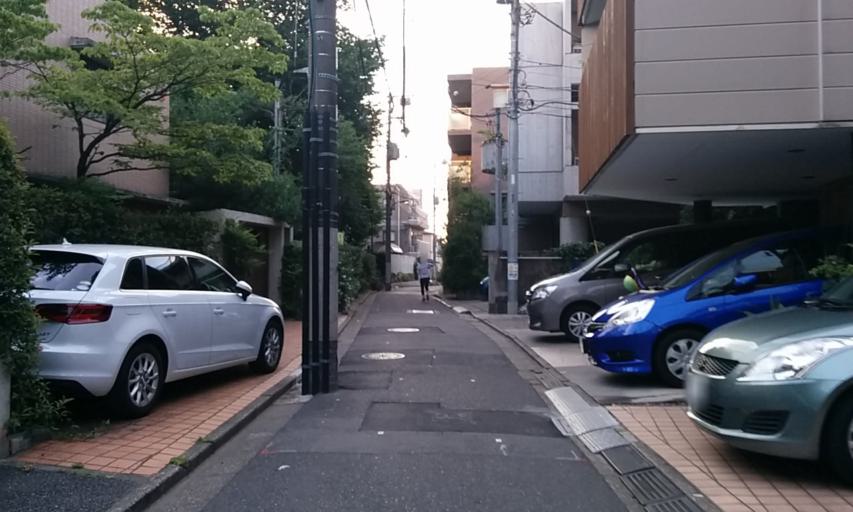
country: JP
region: Tokyo
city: Tokyo
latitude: 35.7106
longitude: 139.7016
